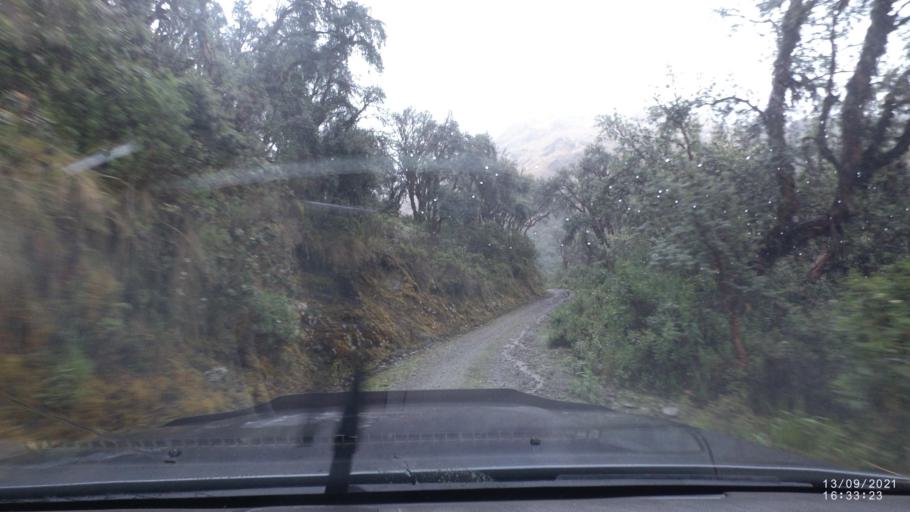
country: BO
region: Cochabamba
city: Colomi
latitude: -17.2772
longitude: -65.7128
